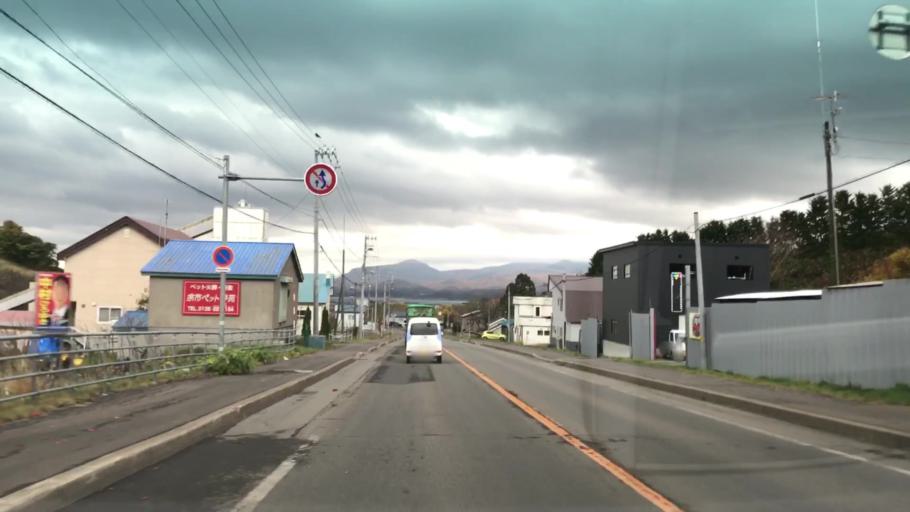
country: JP
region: Hokkaido
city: Yoichi
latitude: 43.2108
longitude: 140.7523
